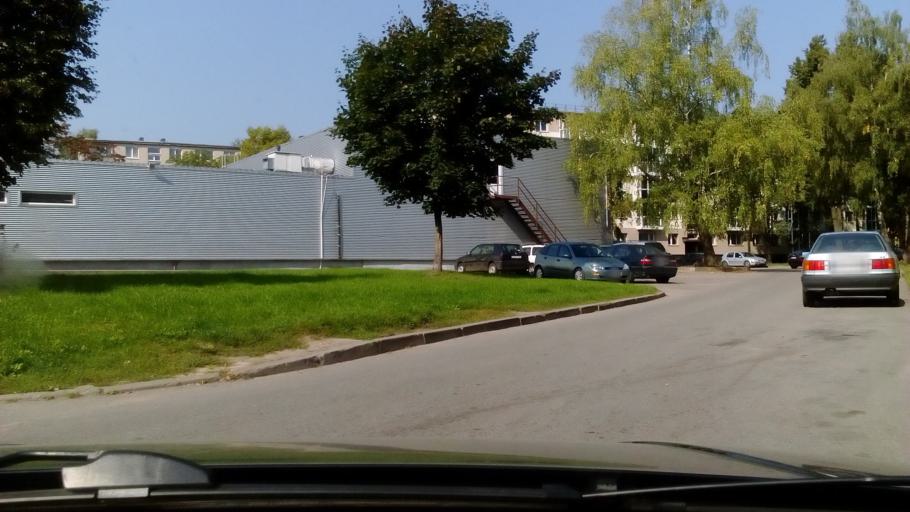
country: LT
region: Alytaus apskritis
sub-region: Alytus
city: Alytus
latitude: 54.3979
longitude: 24.0344
